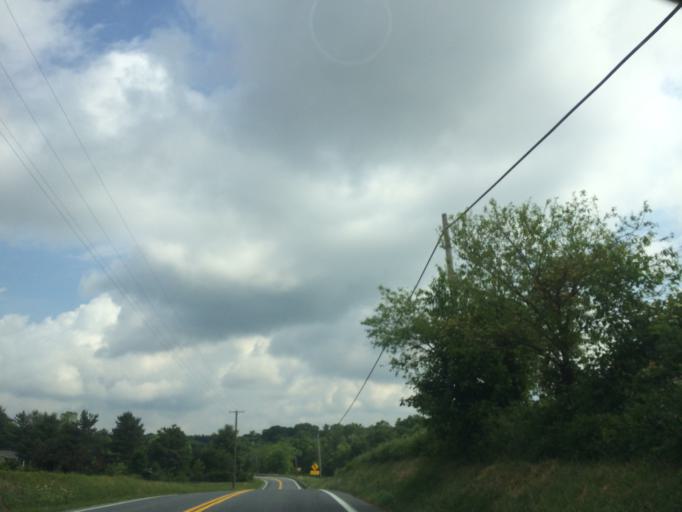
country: US
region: Maryland
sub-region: Carroll County
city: Sykesville
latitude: 39.3915
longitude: -77.0181
